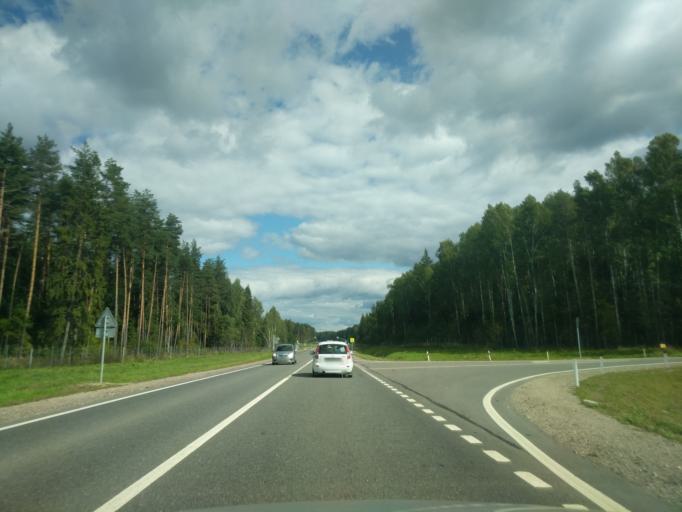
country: RU
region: Kostroma
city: Oktyabr'skiy
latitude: 57.7983
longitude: 41.2431
